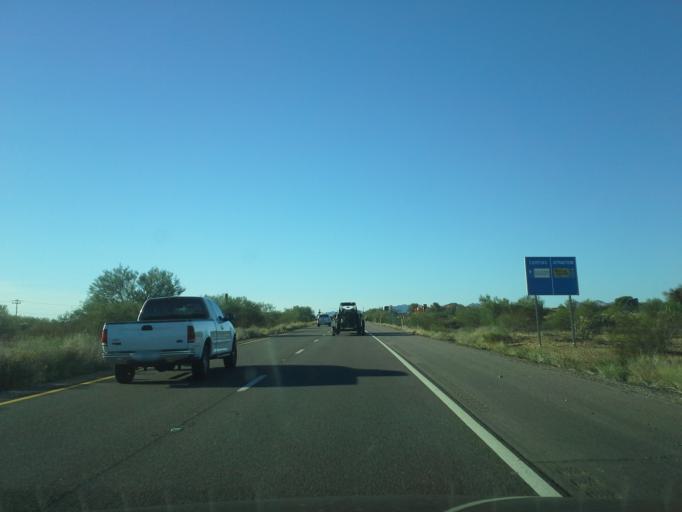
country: US
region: Arizona
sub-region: Pinal County
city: Apache Junction
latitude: 33.3479
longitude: -111.4534
